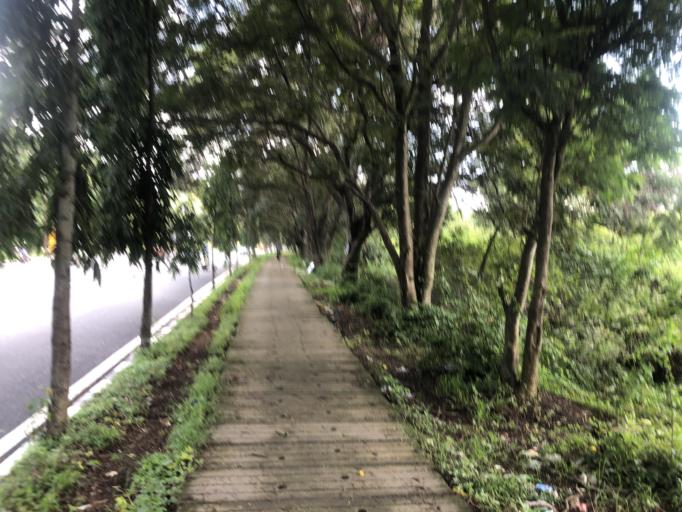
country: IN
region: Karnataka
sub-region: Bangalore Urban
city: Bangalore
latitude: 12.9376
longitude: 77.5107
